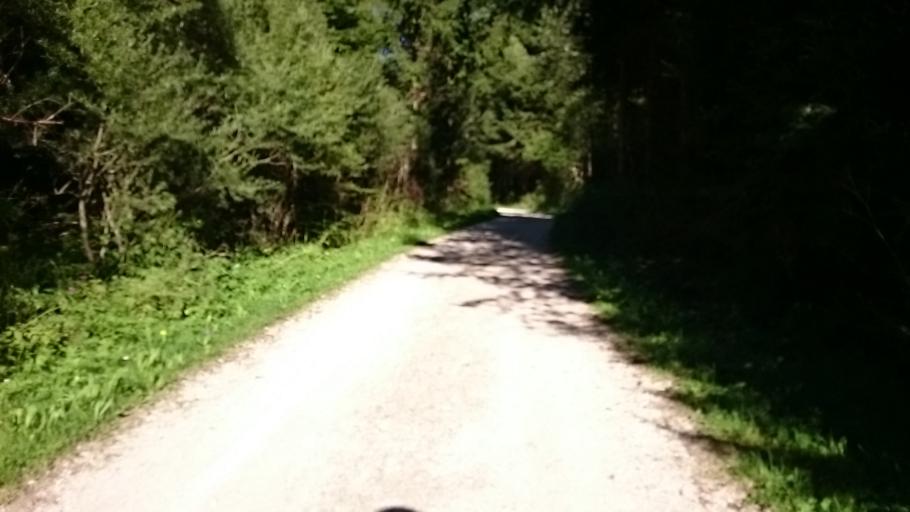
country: IT
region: Trentino-Alto Adige
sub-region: Bolzano
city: Monguelfo
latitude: 46.7595
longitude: 12.0868
